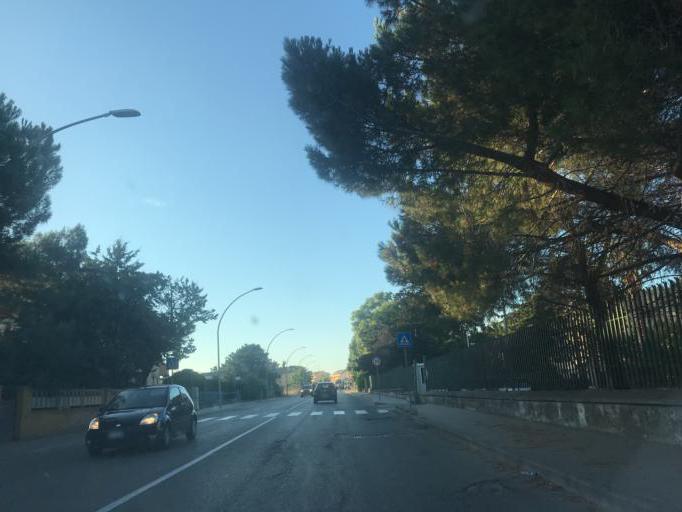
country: IT
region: Sardinia
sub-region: Provincia di Sassari
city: Alghero
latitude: 40.5797
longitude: 8.3188
